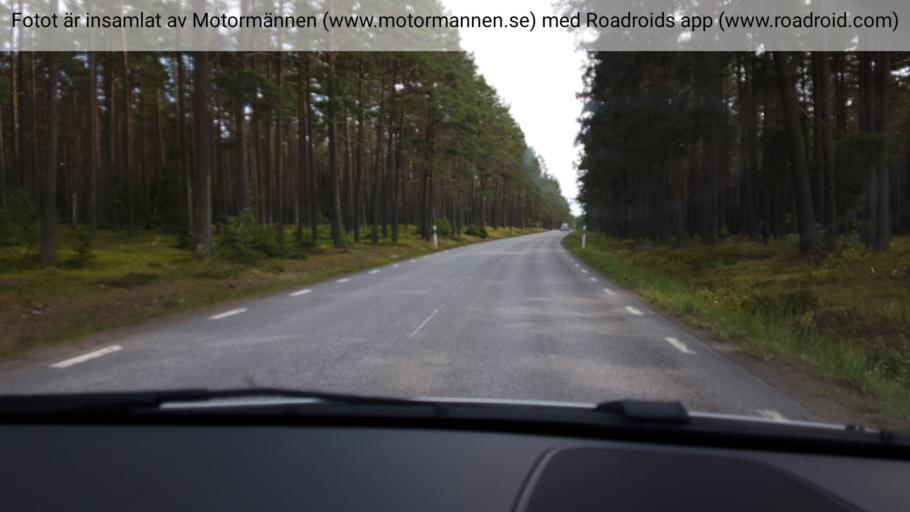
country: SE
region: Uppsala
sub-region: Osthammars Kommun
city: OEsthammar
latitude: 60.2055
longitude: 18.3736
